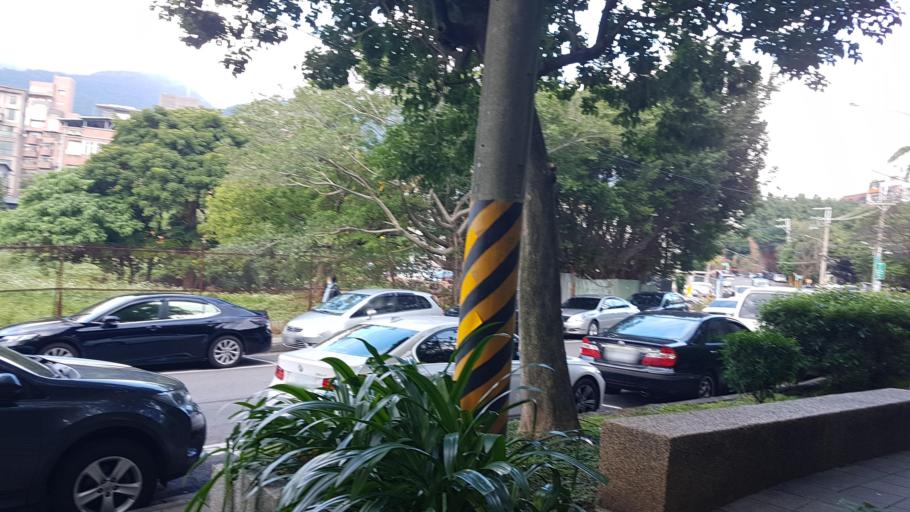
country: TW
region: Taipei
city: Taipei
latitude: 25.1402
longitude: 121.5039
